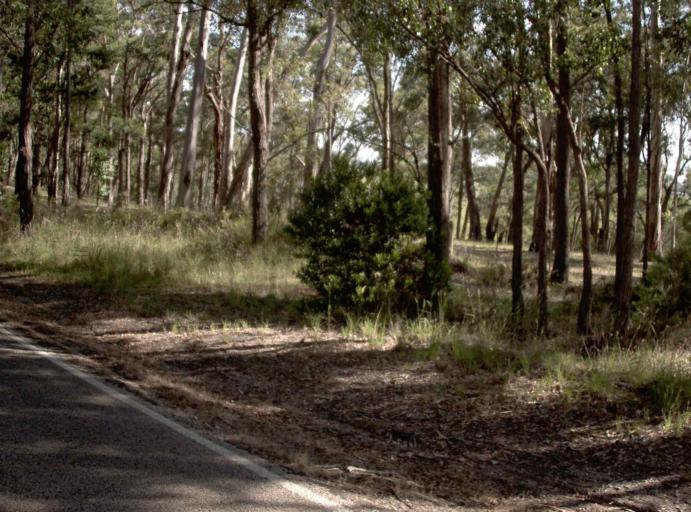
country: AU
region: Victoria
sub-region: East Gippsland
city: Lakes Entrance
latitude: -37.7768
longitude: 147.8195
